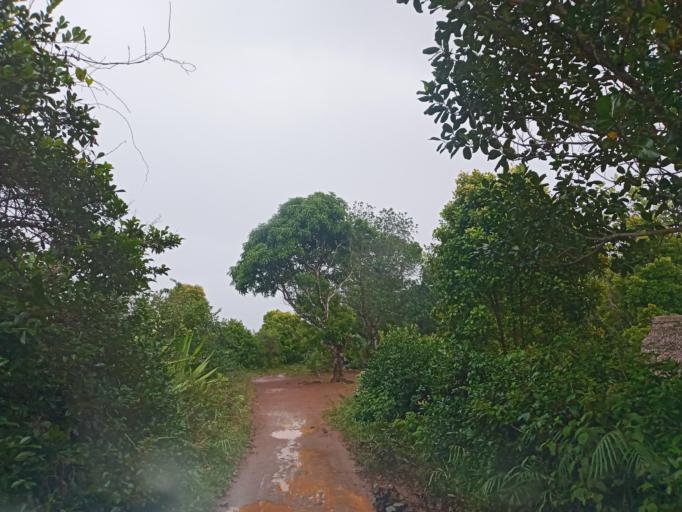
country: MG
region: Atsimo-Atsinanana
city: Vohipaho
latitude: -23.8346
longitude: 47.5488
